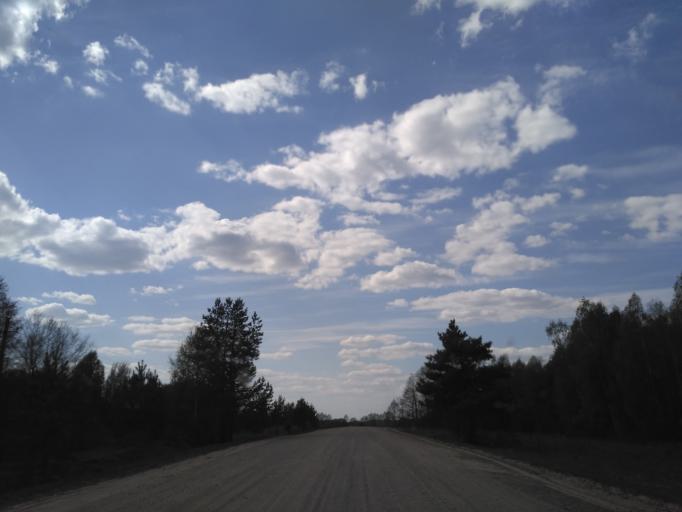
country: BY
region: Minsk
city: Narach
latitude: 54.9935
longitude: 26.5665
